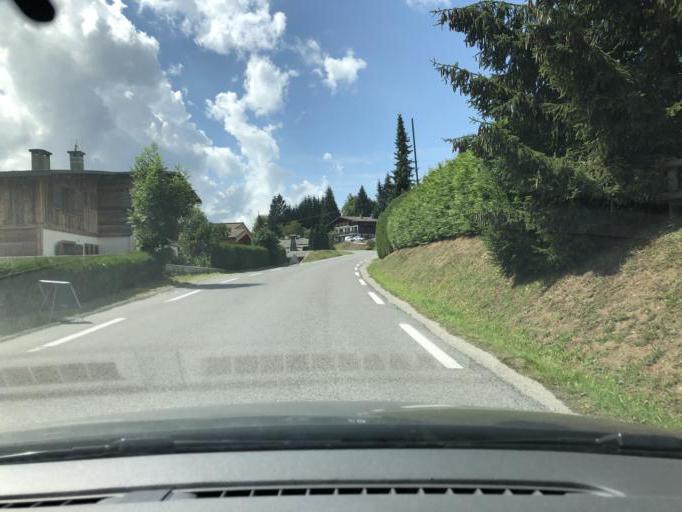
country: FR
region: Rhone-Alpes
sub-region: Departement de la Haute-Savoie
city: Combloux
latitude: 45.8819
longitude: 6.6334
